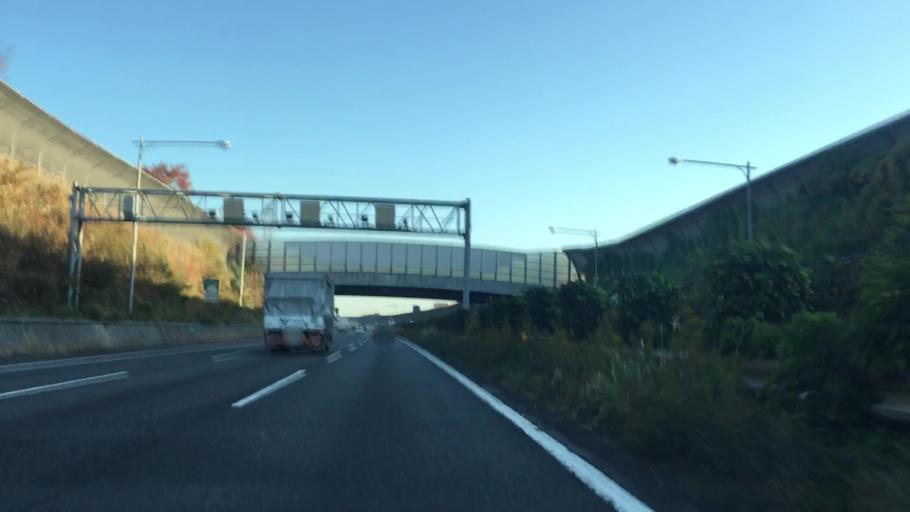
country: JP
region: Kanagawa
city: Isehara
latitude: 35.3870
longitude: 139.2771
